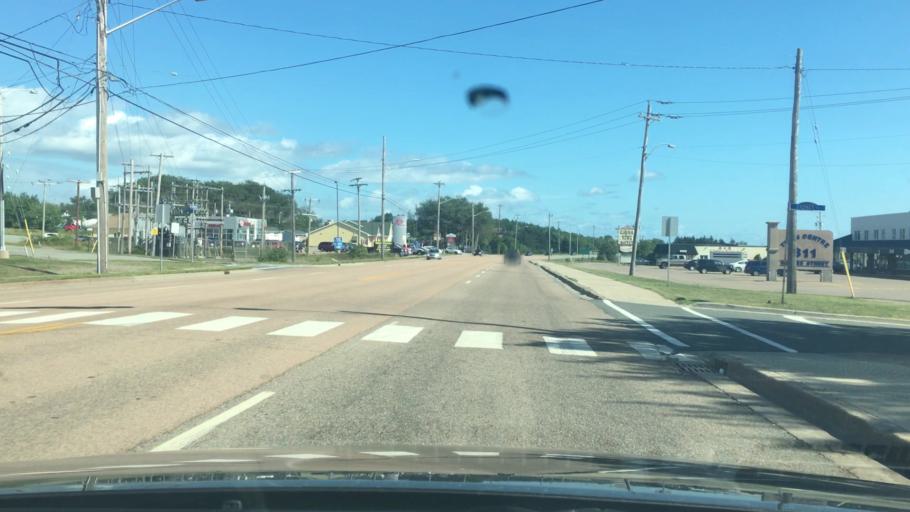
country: CA
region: Nova Scotia
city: Port Hawkesbury
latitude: 45.6142
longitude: -61.3499
